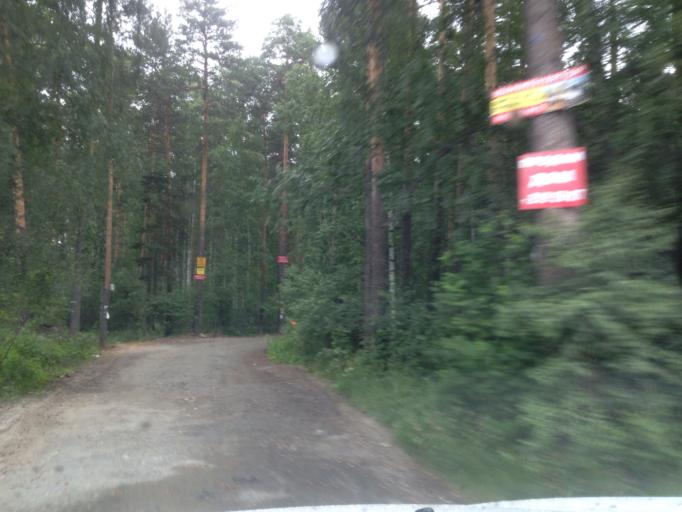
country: RU
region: Sverdlovsk
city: Istok
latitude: 56.8395
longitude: 60.8026
